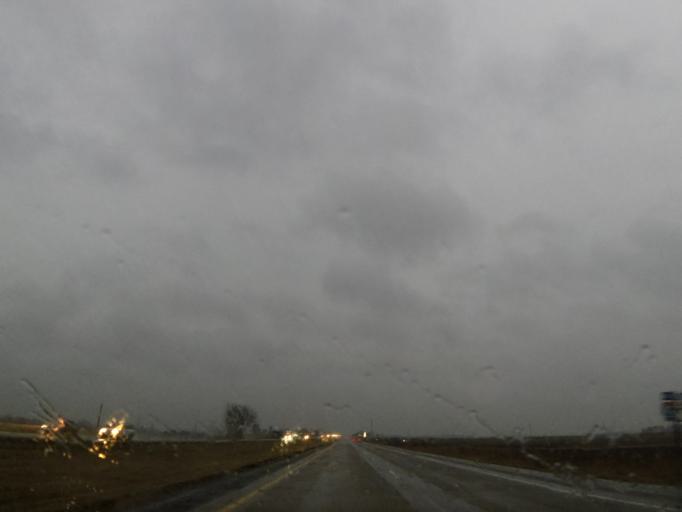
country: US
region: Iowa
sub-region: Cerro Gordo County
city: Clear Lake
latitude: 43.2064
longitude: -93.3488
